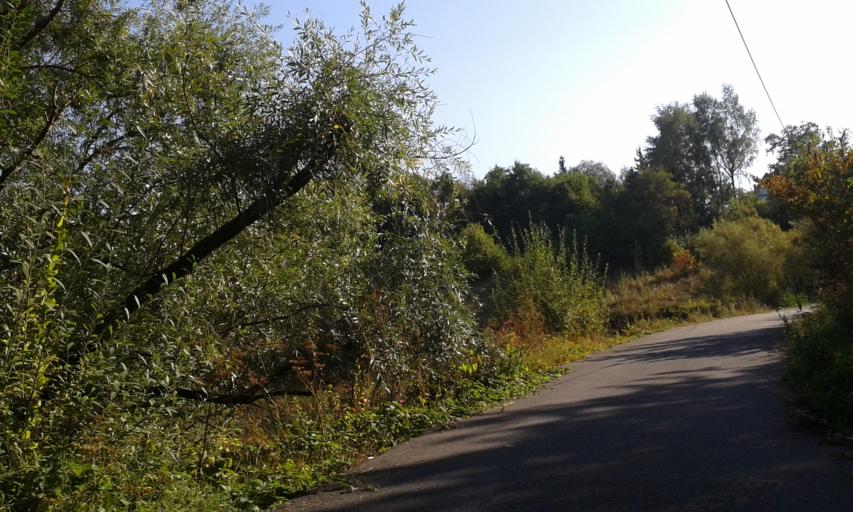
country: DE
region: Bavaria
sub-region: Upper Franconia
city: Bamberg
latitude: 49.8718
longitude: 10.8852
